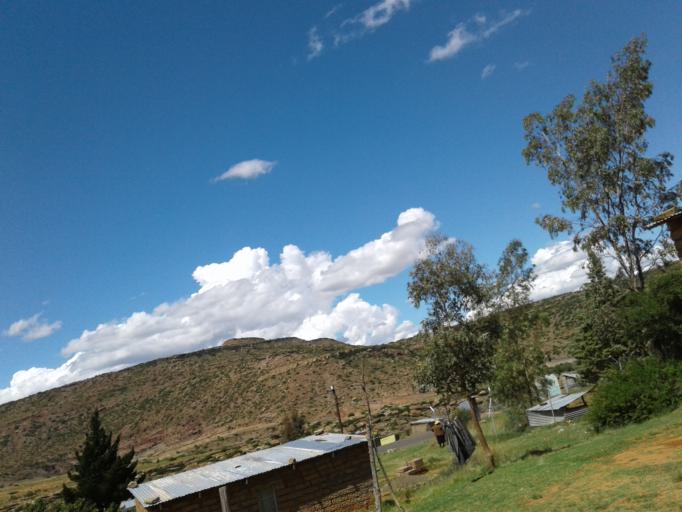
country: LS
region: Quthing
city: Quthing
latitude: -30.3631
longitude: 27.5486
